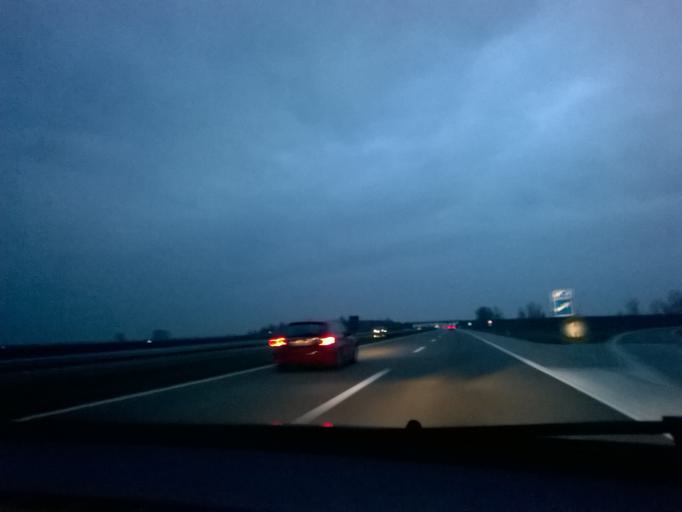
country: RS
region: Autonomna Pokrajina Vojvodina
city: Nova Pazova
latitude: 44.9911
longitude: 20.2112
